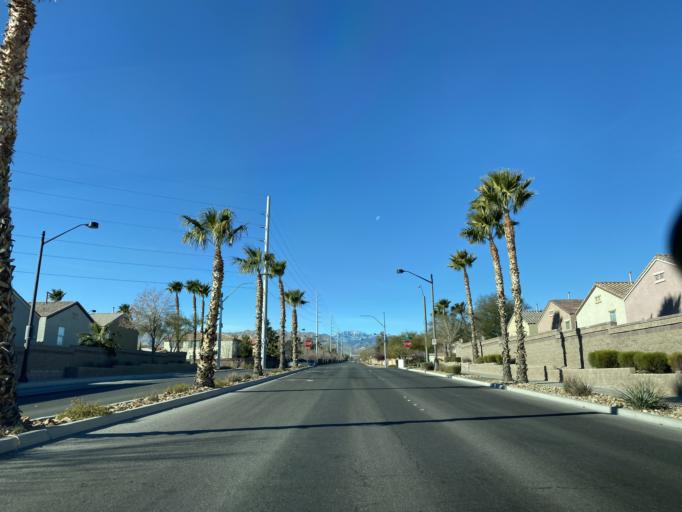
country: US
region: Nevada
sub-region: Clark County
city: Summerlin South
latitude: 36.2992
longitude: -115.2958
